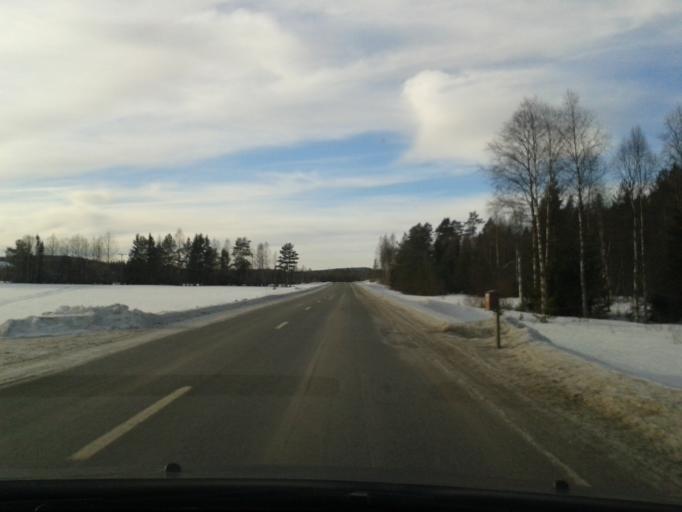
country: SE
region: Vaesternorrland
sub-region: OErnskoeldsviks Kommun
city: Bredbyn
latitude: 63.5272
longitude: 18.0045
